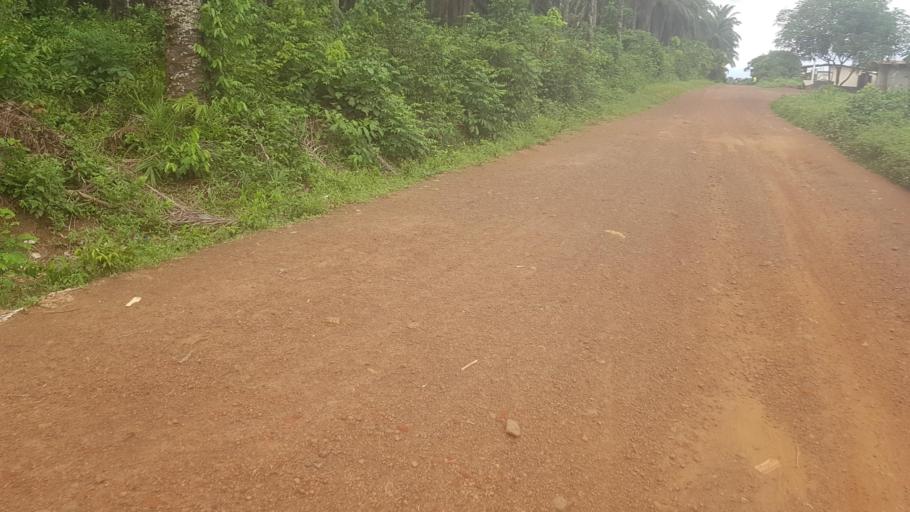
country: SL
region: Southern Province
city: Mogbwemo
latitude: 7.5979
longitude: -12.1747
